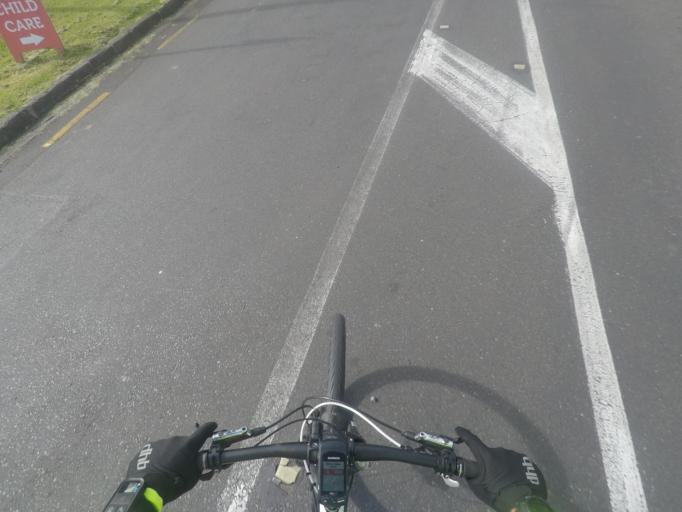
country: NZ
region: Auckland
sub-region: Auckland
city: Auckland
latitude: -36.9162
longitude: 174.7822
